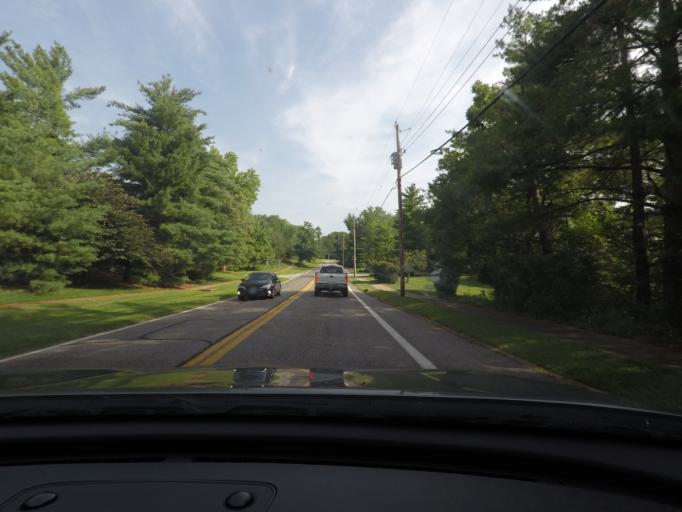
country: US
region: Missouri
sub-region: Saint Louis County
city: Town and Country
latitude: 38.6240
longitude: -90.4829
